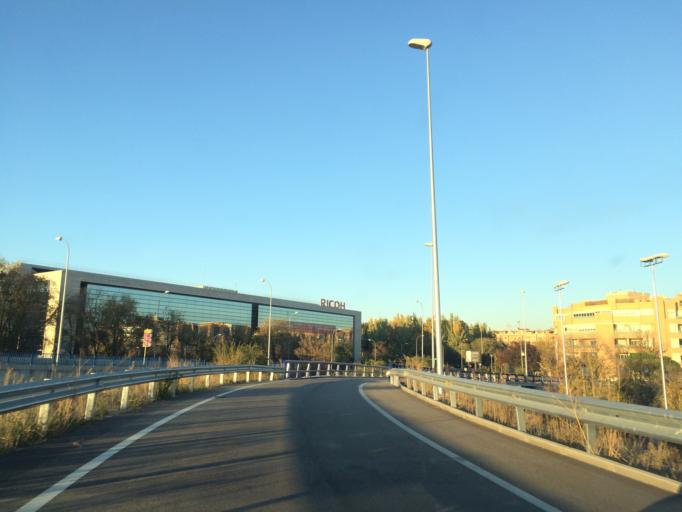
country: ES
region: Madrid
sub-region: Provincia de Madrid
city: Alcobendas
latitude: 40.5346
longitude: -3.6401
